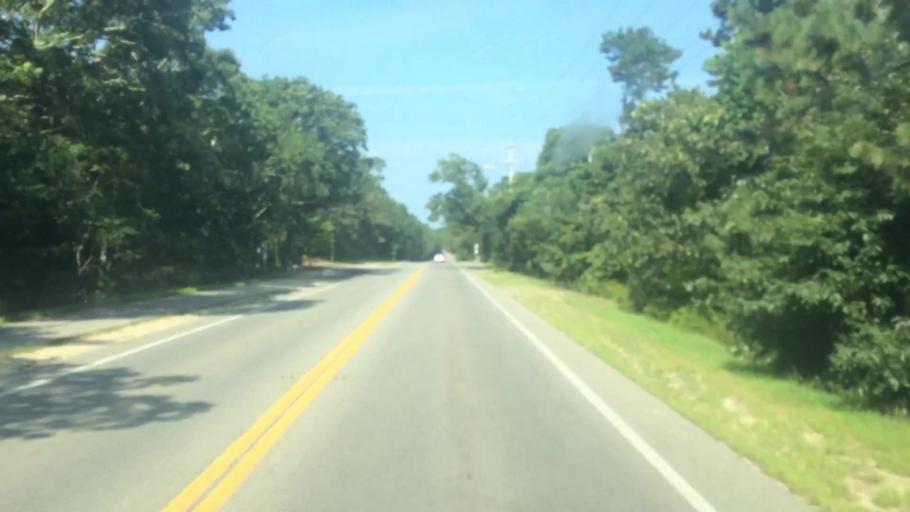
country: US
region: Massachusetts
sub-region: Dukes County
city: Oak Bluffs
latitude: 41.4108
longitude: -70.5730
